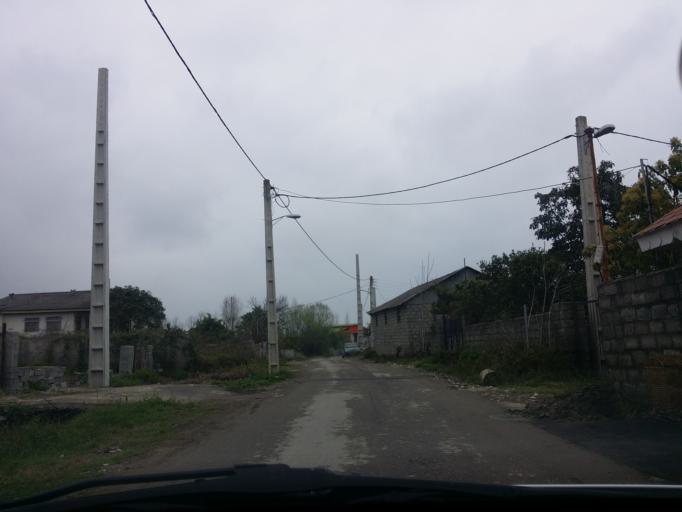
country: IR
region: Mazandaran
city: Chalus
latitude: 36.6694
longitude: 51.3790
